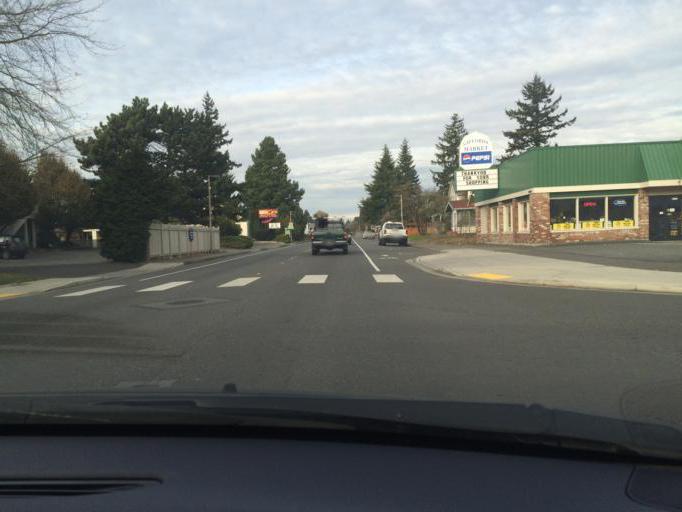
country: US
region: Washington
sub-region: Whatcom County
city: Bellingham
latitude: 48.7618
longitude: -122.4884
